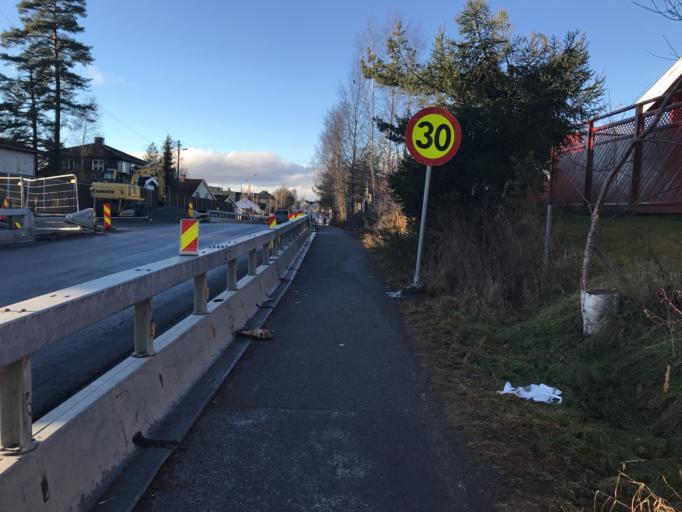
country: NO
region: Akershus
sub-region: Ullensaker
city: Jessheim
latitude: 60.1407
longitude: 11.1837
